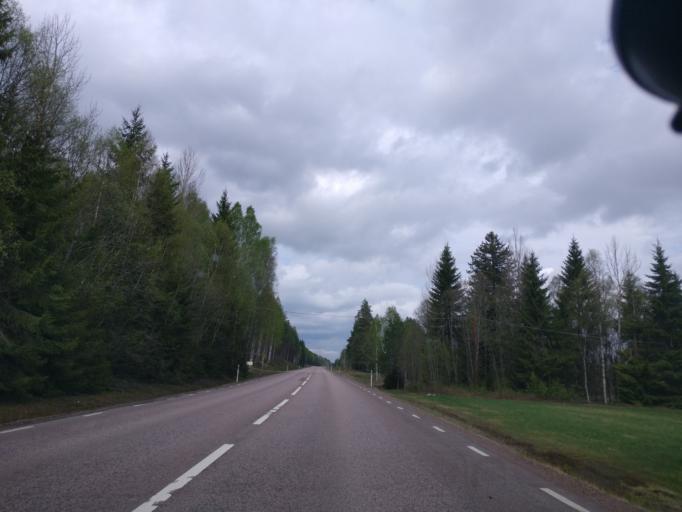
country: SE
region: Vaermland
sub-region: Hagfors Kommun
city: Ekshaerad
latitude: 60.1442
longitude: 13.5241
